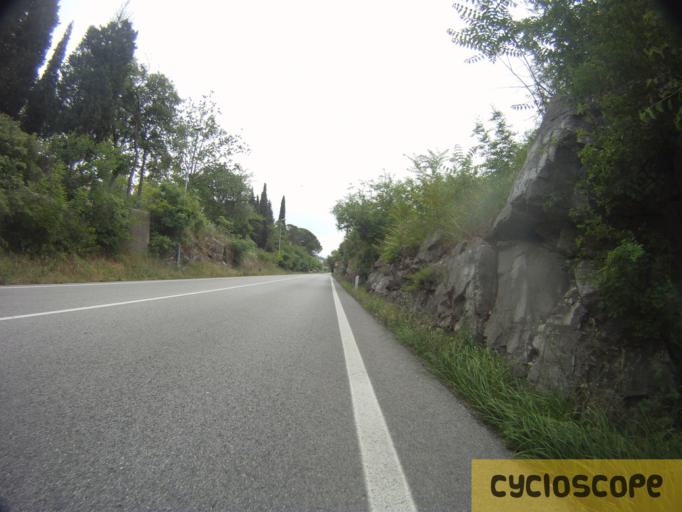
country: IT
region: Friuli Venezia Giulia
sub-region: Provincia di Trieste
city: Duino
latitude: 45.7909
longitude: 13.5876
